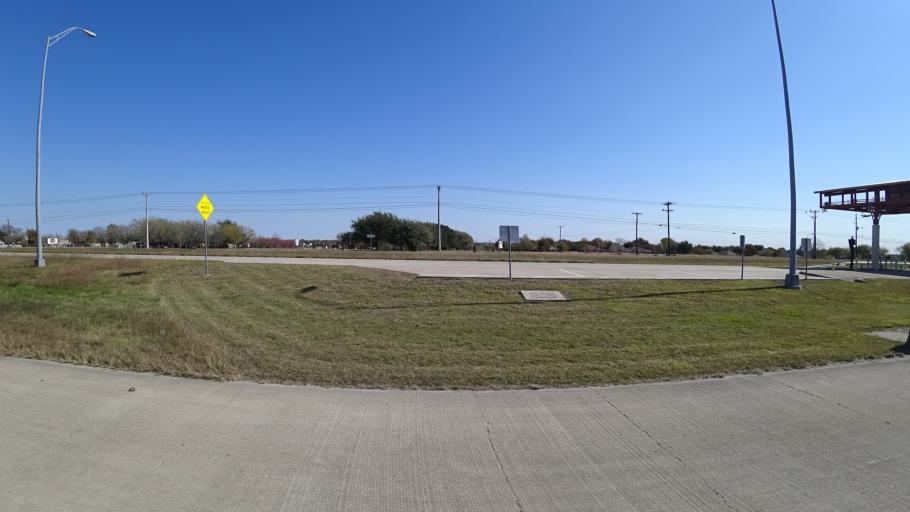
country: US
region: Texas
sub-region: Williamson County
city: Hutto
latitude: 30.4947
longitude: -97.5828
